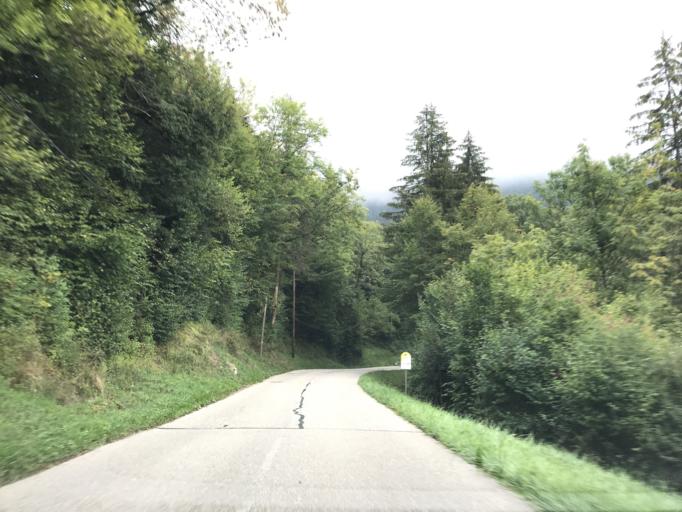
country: FR
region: Rhone-Alpes
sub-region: Departement de la Haute-Savoie
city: Talloires
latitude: 45.8333
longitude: 6.2395
